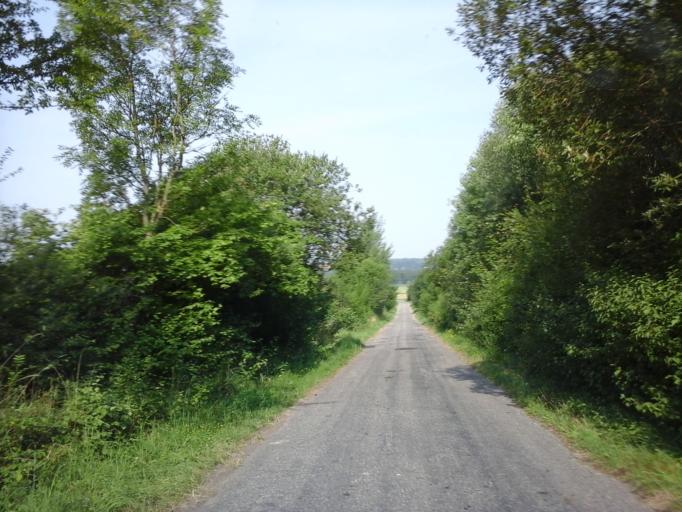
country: PL
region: West Pomeranian Voivodeship
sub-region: Powiat choszczenski
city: Pelczyce
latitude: 53.0664
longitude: 15.2368
